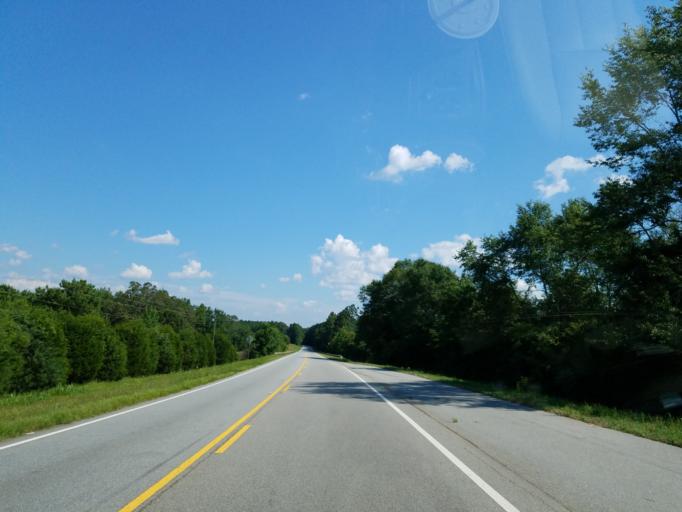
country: US
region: Georgia
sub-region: Crawford County
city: Roberta
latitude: 32.8742
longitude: -84.0906
